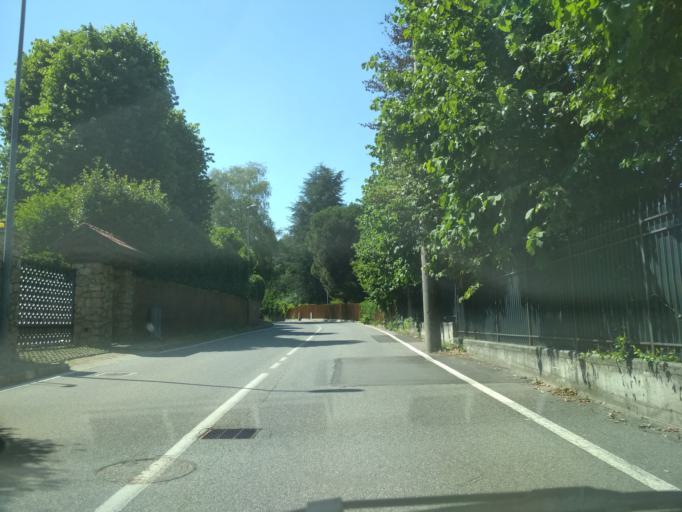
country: IT
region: Piedmont
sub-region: Provincia di Torino
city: Rivoli
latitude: 45.0643
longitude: 7.5027
